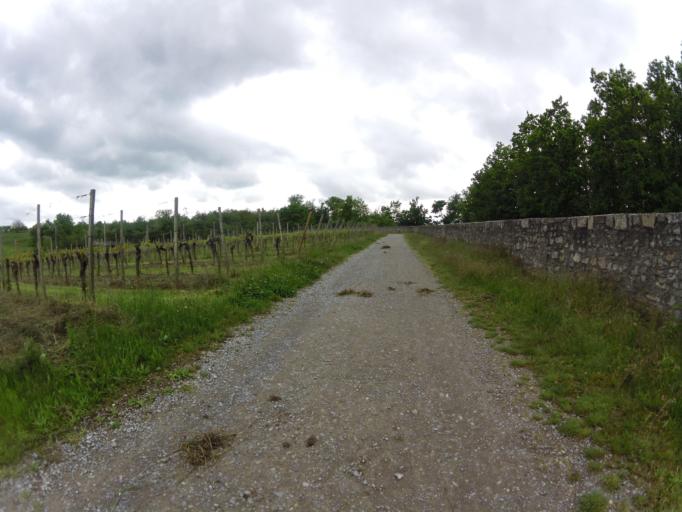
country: DE
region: Bavaria
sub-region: Regierungsbezirk Unterfranken
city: Sommerach
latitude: 49.8507
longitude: 10.2073
